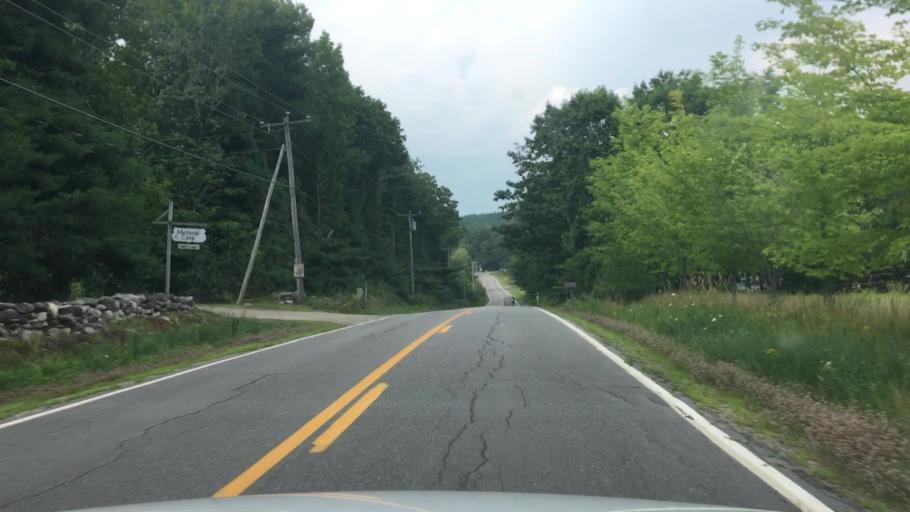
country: US
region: Maine
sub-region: Knox County
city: Washington
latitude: 44.2854
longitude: -69.3656
